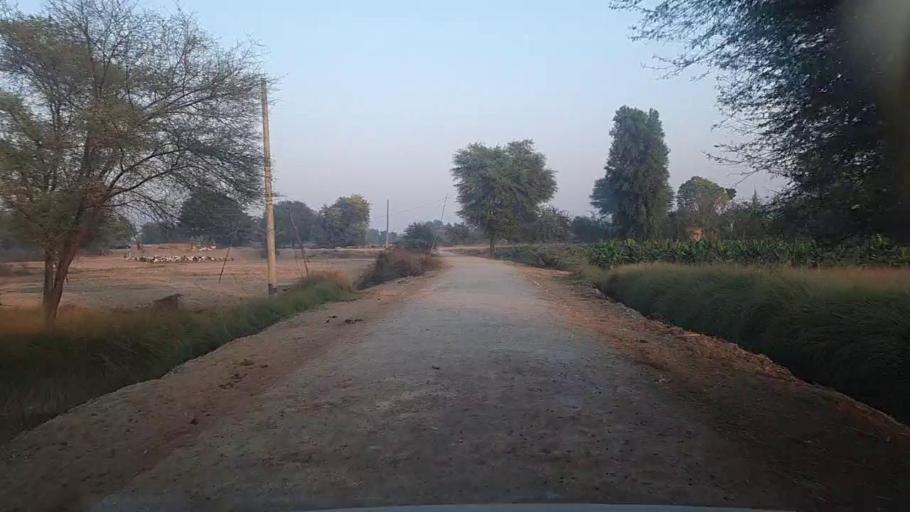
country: PK
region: Sindh
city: Karaundi
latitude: 26.8459
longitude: 68.3700
